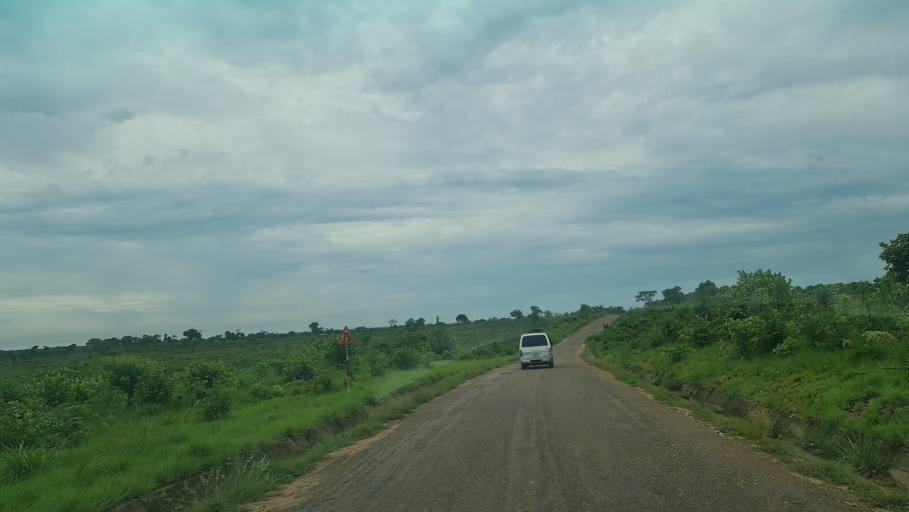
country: MW
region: Southern Region
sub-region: Nsanje District
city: Nsanje
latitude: -17.6810
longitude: 35.7248
